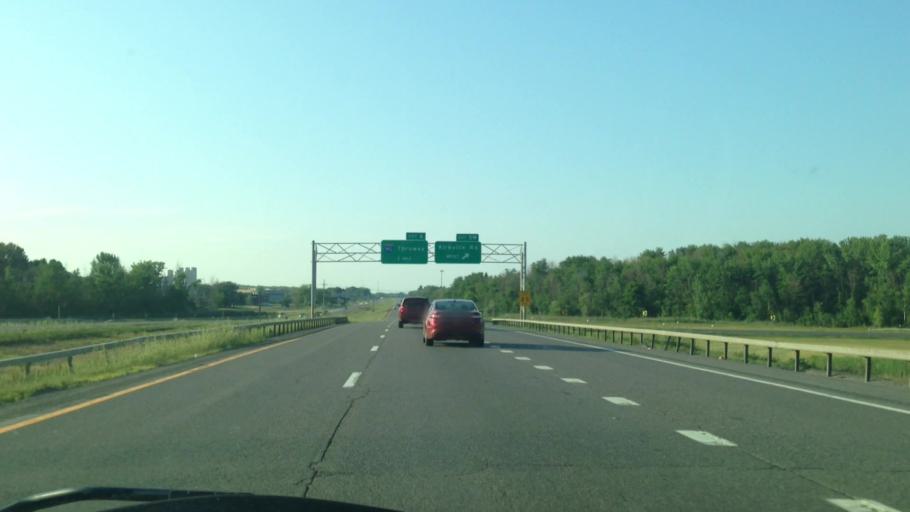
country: US
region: New York
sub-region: Onondaga County
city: East Syracuse
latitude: 43.0782
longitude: -76.0534
